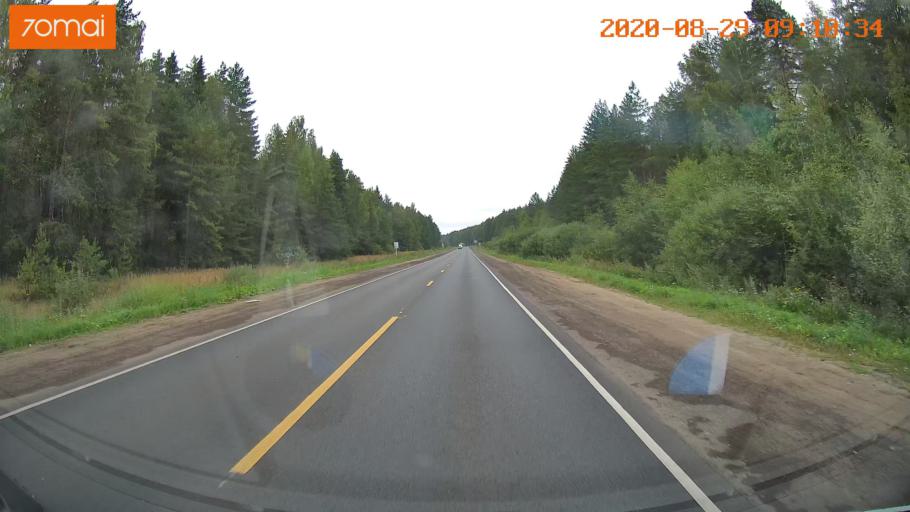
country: RU
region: Ivanovo
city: Kineshma
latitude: 57.4157
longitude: 42.0738
